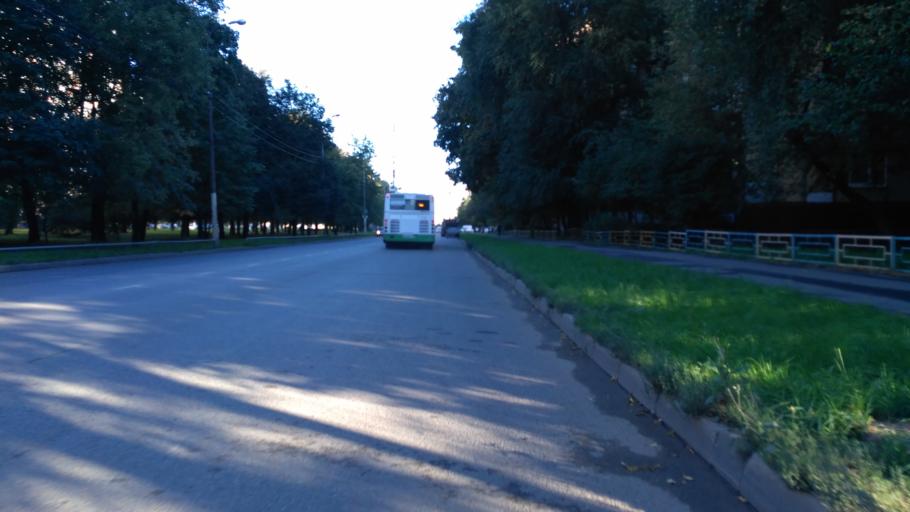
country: RU
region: Moskovskaya
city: Vostochnoe Degunino
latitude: 55.8657
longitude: 37.5595
